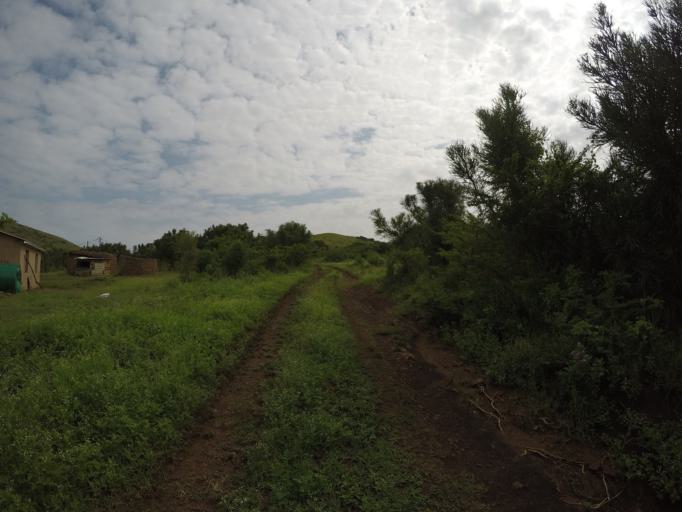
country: ZA
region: KwaZulu-Natal
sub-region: uThungulu District Municipality
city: Empangeni
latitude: -28.6228
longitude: 31.8946
